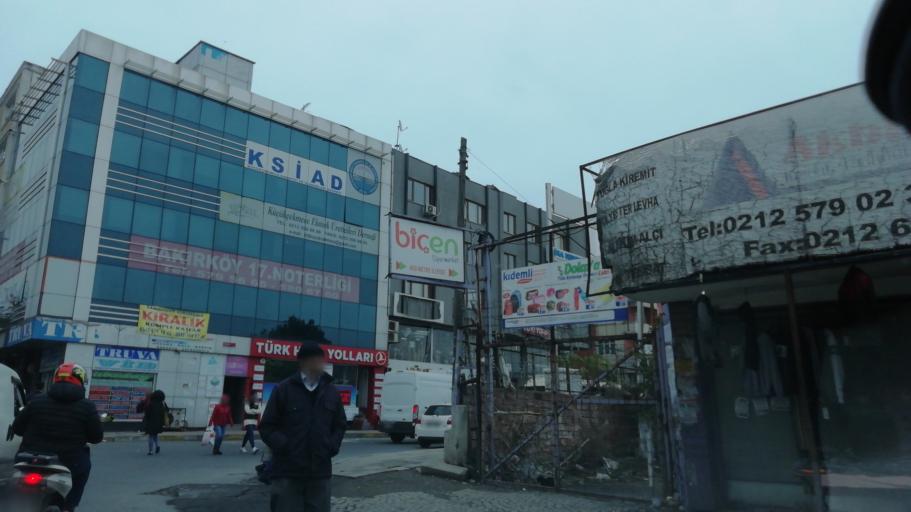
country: TR
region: Istanbul
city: Mahmutbey
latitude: 41.0003
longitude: 28.7972
